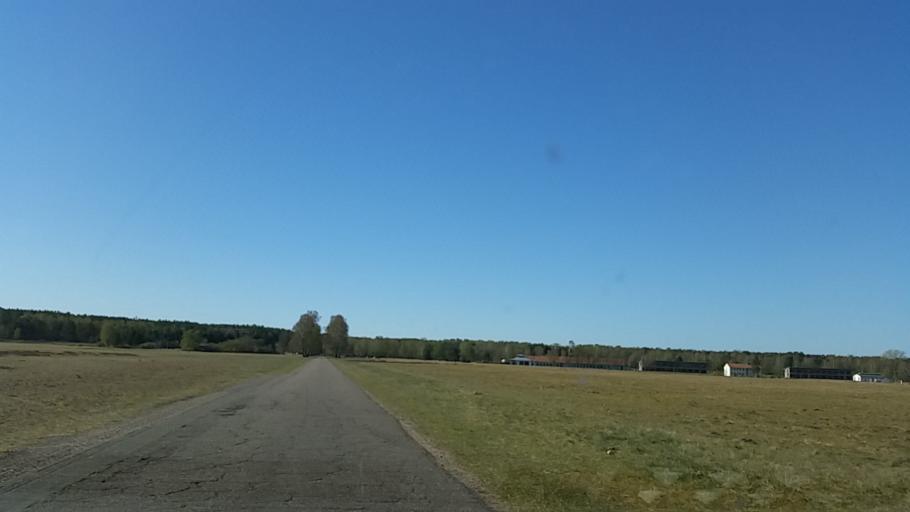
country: DE
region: Lower Saxony
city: Schneverdingen
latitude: 53.1488
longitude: 9.8260
